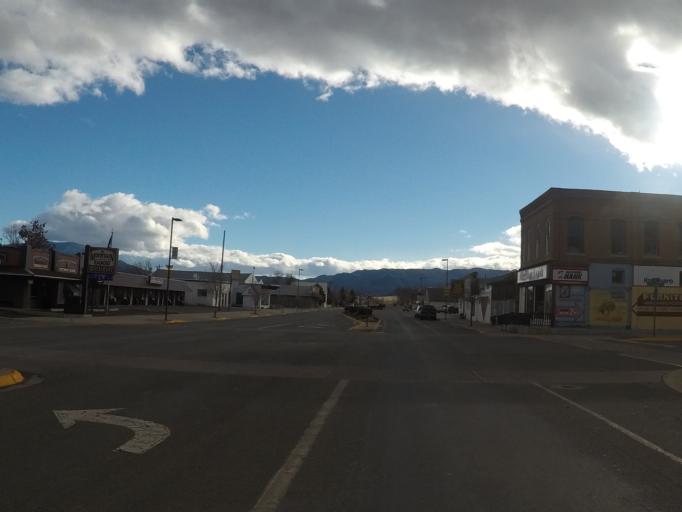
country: US
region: Montana
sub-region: Jefferson County
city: Boulder
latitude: 46.2377
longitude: -112.1189
